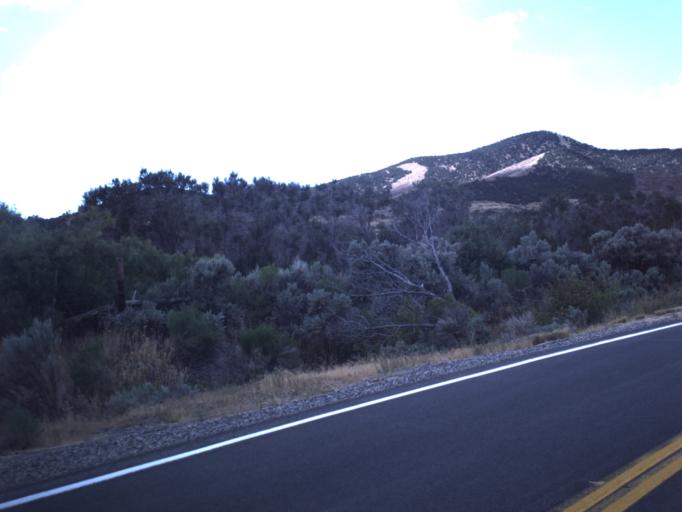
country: US
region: Utah
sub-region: Tooele County
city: Grantsville
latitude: 40.3336
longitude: -112.5230
